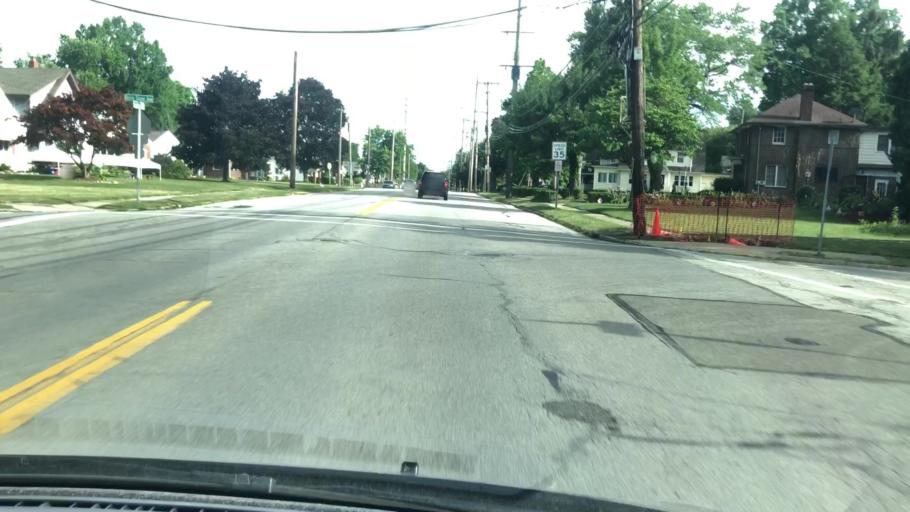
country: US
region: Ohio
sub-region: Summit County
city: Silver Lake
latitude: 41.1542
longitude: -81.4752
